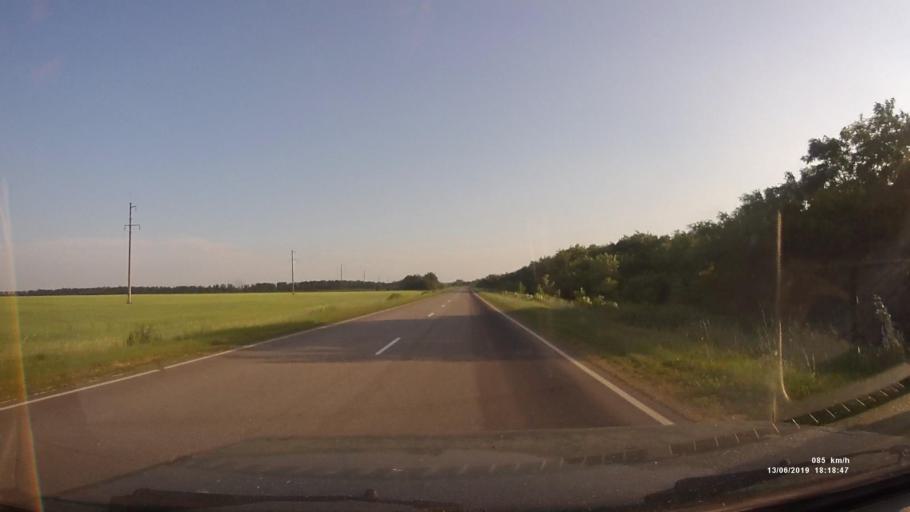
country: RU
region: Rostov
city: Kazanskaya
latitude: 49.9043
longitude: 41.3108
